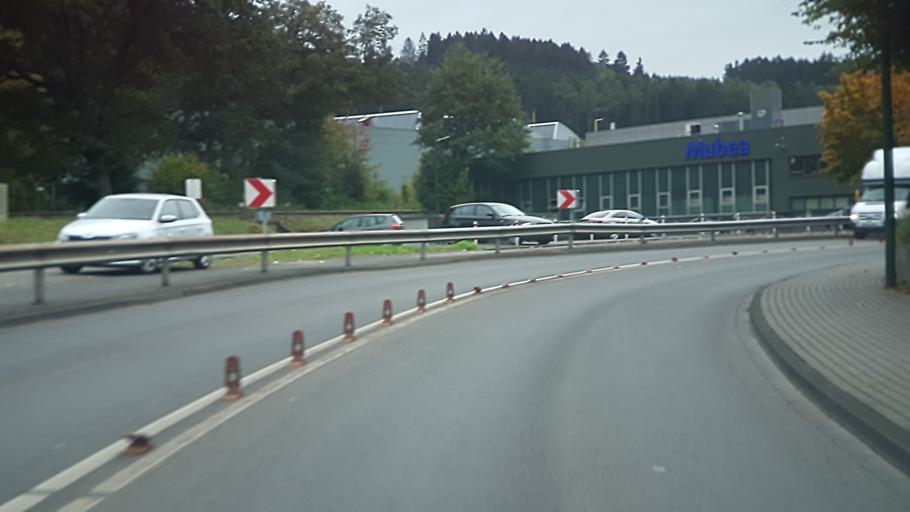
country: DE
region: North Rhine-Westphalia
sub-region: Regierungsbezirk Arnsberg
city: Attendorn
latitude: 51.1192
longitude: 7.9002
